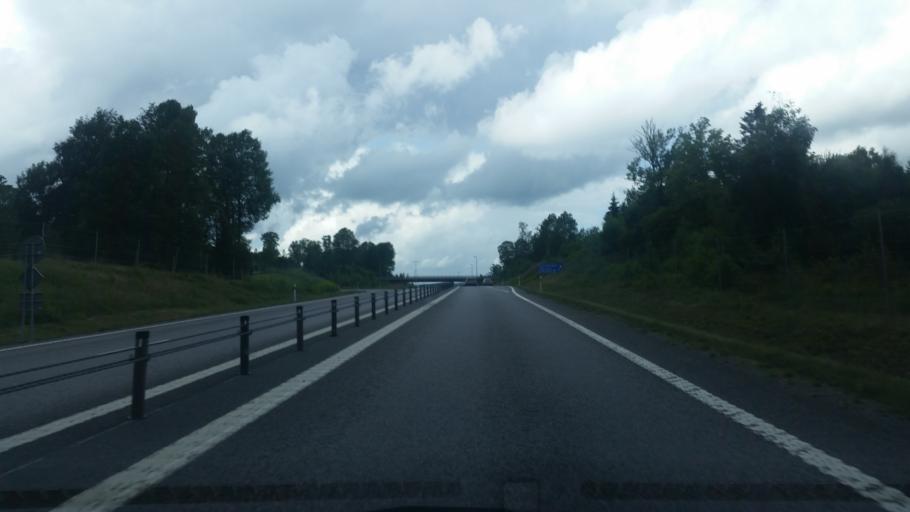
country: SE
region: Vaestra Goetaland
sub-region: Boras Kommun
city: Dalsjofors
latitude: 57.6467
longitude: 13.0657
